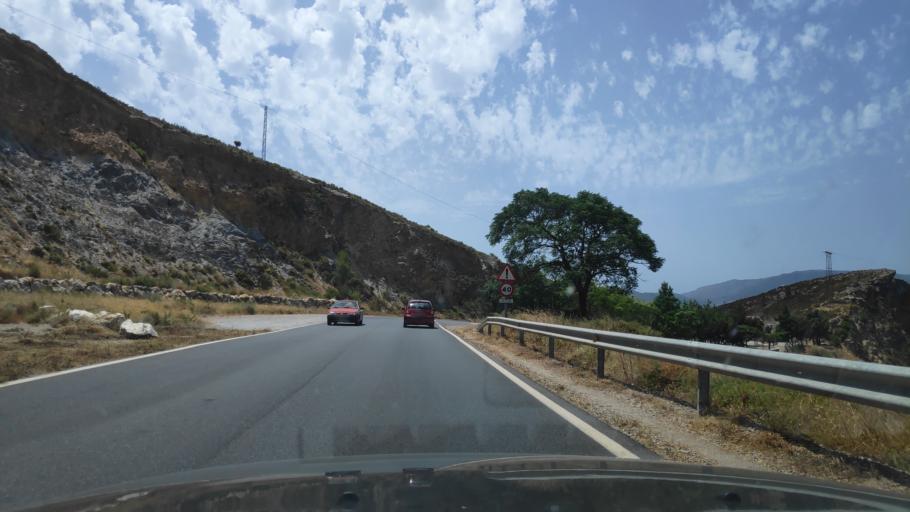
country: ES
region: Andalusia
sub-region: Provincia de Granada
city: Lanjaron
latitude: 36.9136
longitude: -3.4749
